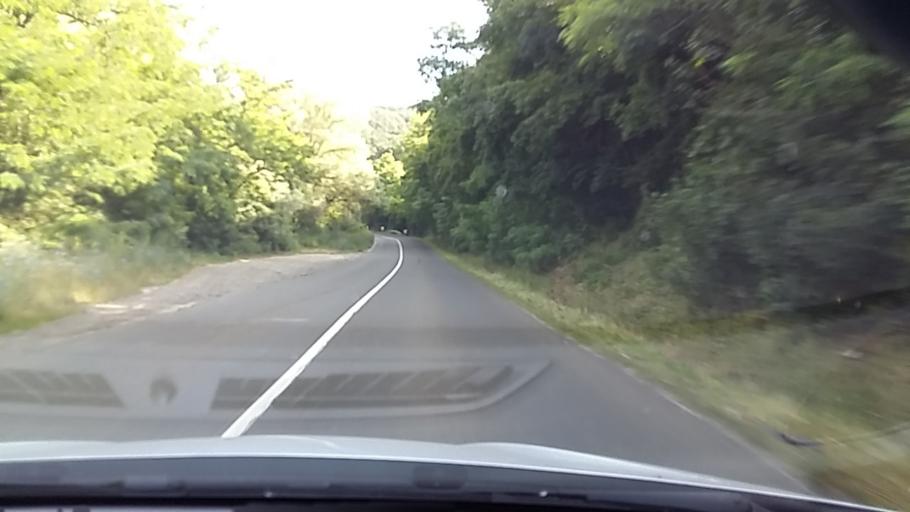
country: HU
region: Pest
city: Szob
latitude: 47.8477
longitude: 18.8229
